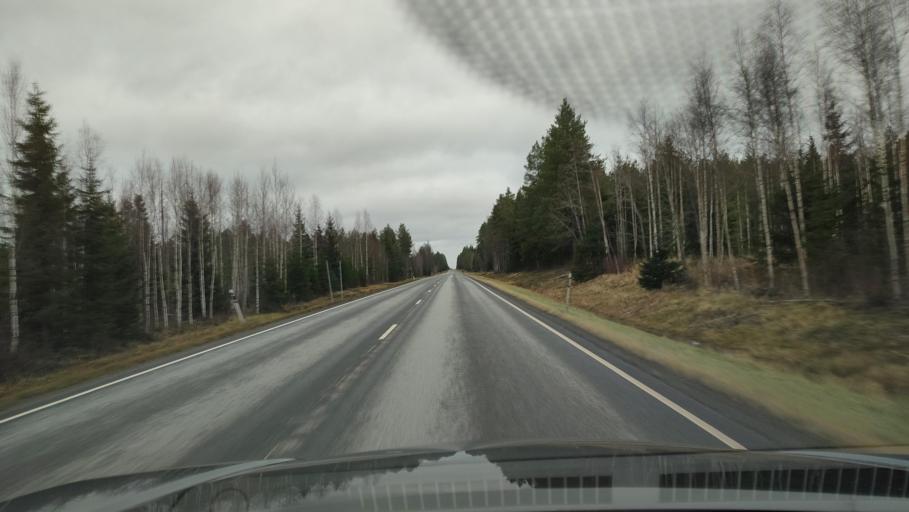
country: FI
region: Southern Ostrobothnia
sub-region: Seinaejoki
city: Kurikka
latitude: 62.5243
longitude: 22.3217
